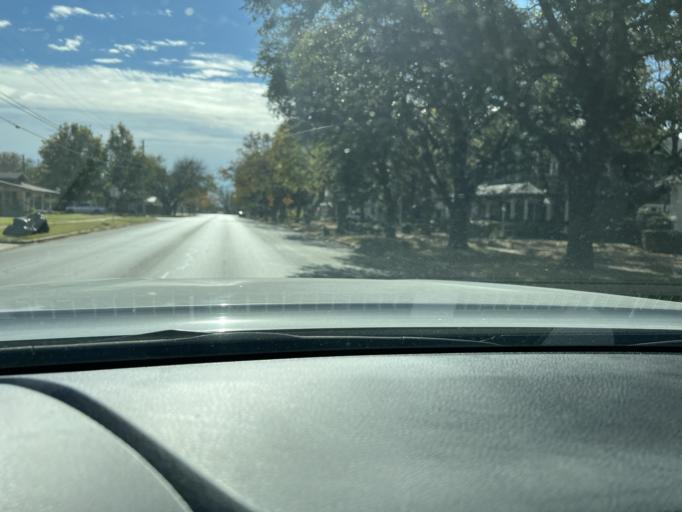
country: US
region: Texas
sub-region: Eastland County
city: Eastland
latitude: 32.3909
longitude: -98.8181
